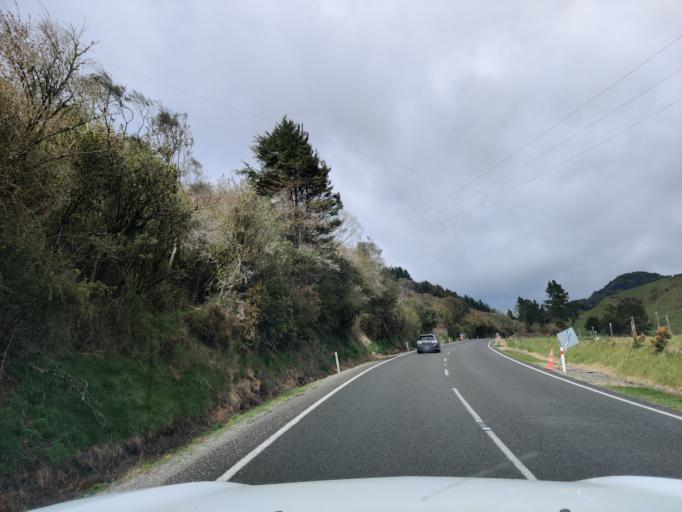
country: NZ
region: Waikato
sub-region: Otorohanga District
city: Otorohanga
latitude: -38.6162
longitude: 175.2191
